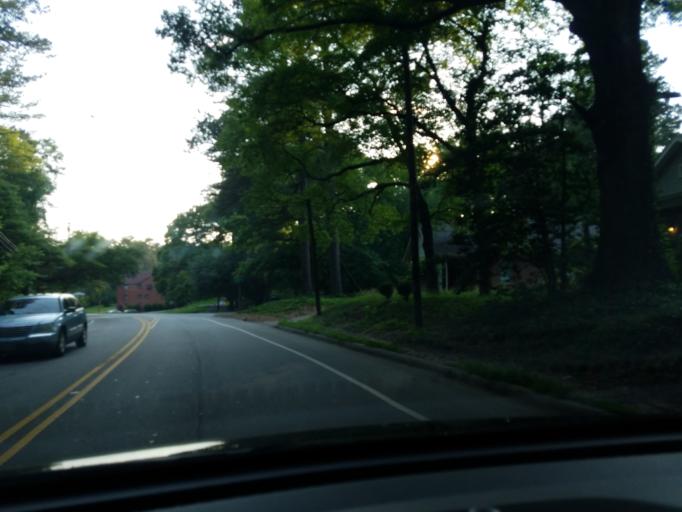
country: US
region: North Carolina
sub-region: Durham County
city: Durham
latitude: 35.9766
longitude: -78.9200
